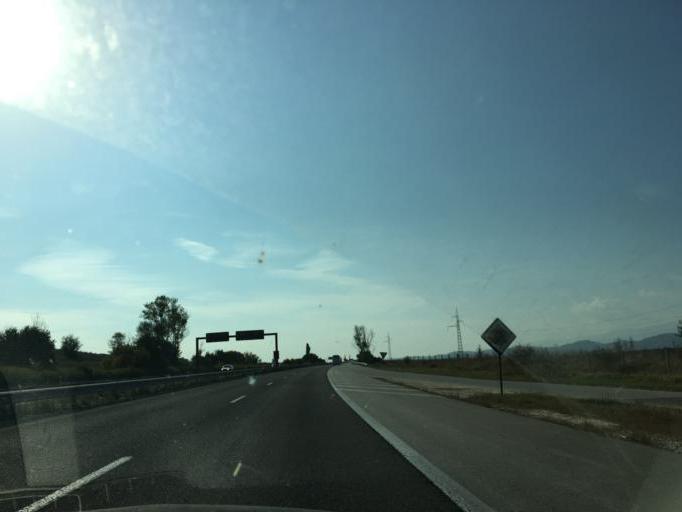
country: BG
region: Sofiya
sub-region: Obshtina Ikhtiman
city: Ikhtiman
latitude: 42.4854
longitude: 23.7898
